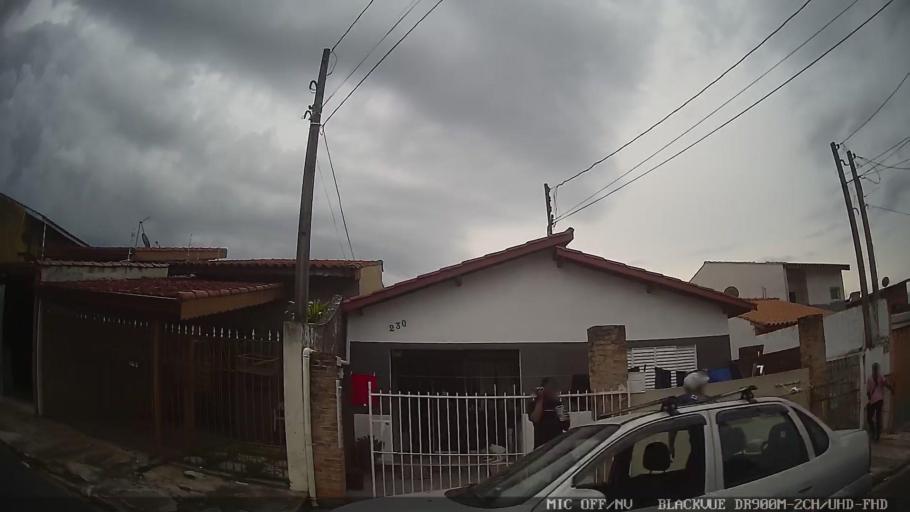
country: BR
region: Sao Paulo
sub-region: Atibaia
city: Atibaia
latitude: -23.1329
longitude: -46.5641
